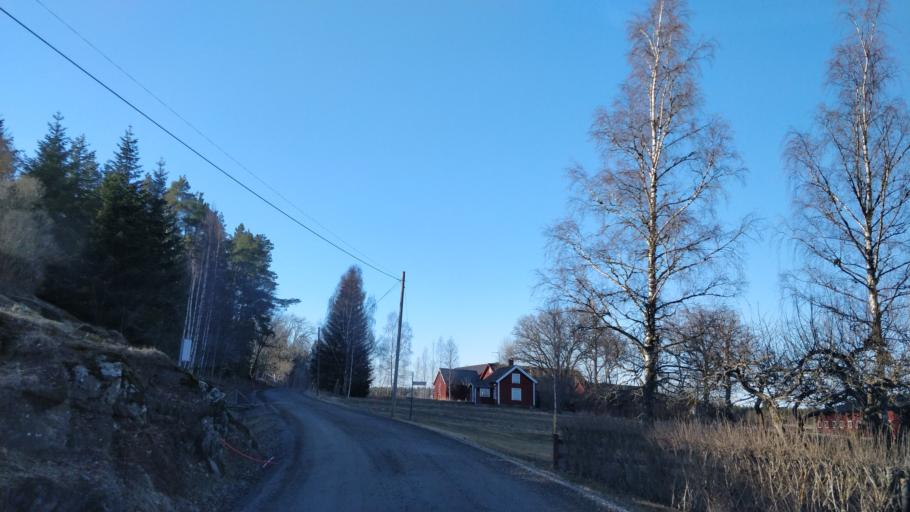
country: SE
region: Uppsala
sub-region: Enkopings Kommun
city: Orsundsbro
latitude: 59.7552
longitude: 17.1711
